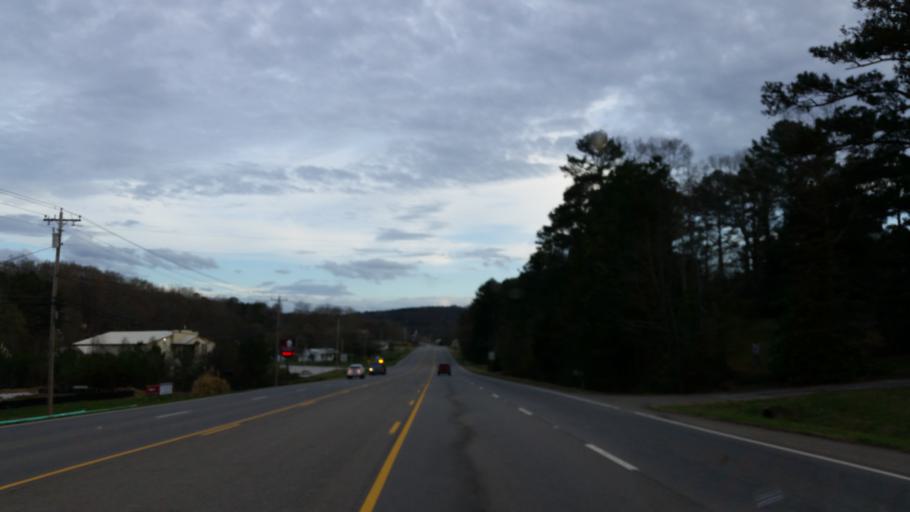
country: US
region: Georgia
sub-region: Gordon County
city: Calhoun
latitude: 34.4645
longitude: -84.9120
